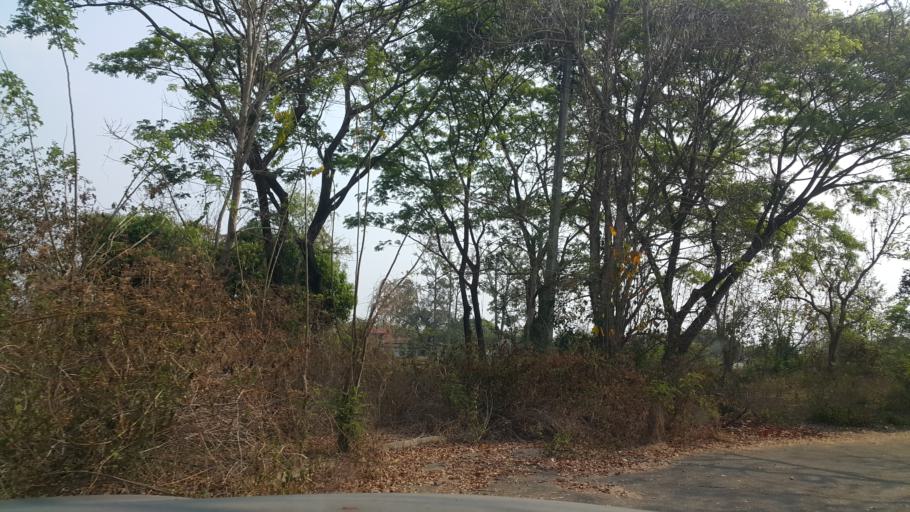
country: TH
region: Chiang Mai
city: San Kamphaeng
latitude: 18.7638
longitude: 99.1112
